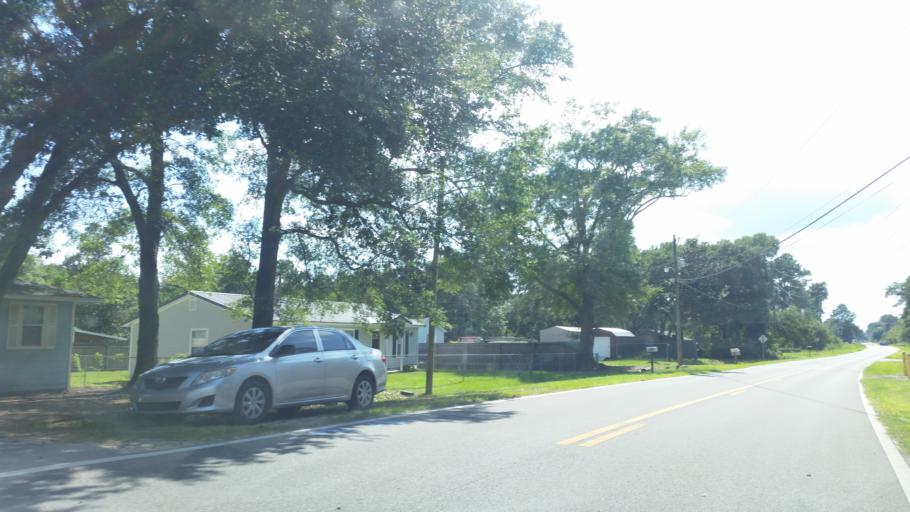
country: US
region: Florida
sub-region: Santa Rosa County
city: Pace
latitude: 30.5891
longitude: -87.1451
